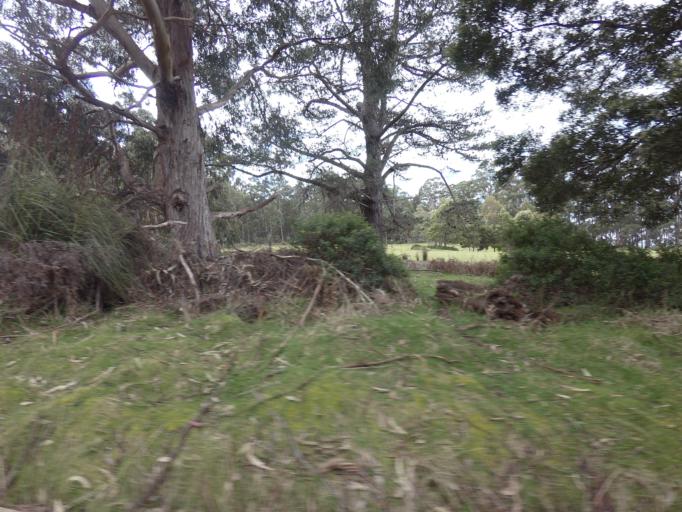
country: AU
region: Tasmania
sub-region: Huon Valley
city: Geeveston
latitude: -43.4057
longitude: 147.0142
